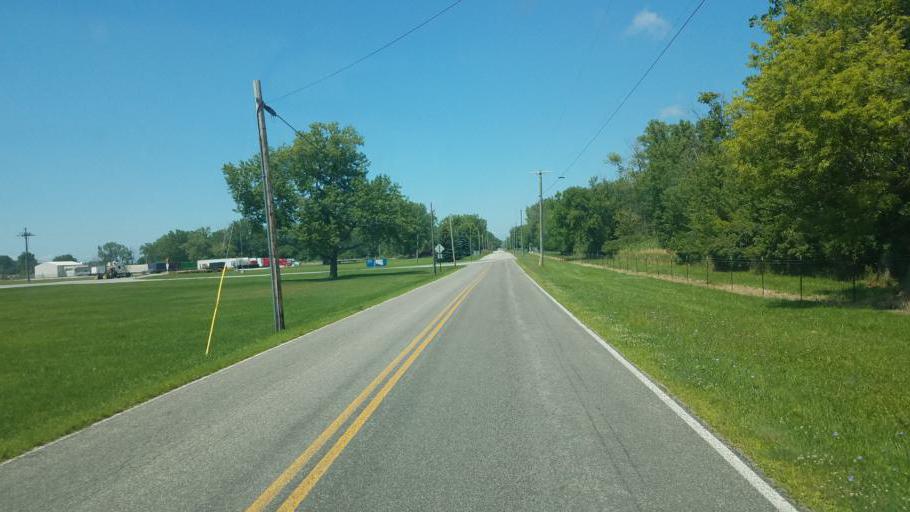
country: US
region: Ohio
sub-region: Ottawa County
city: Port Clinton
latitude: 41.4922
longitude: -82.8709
